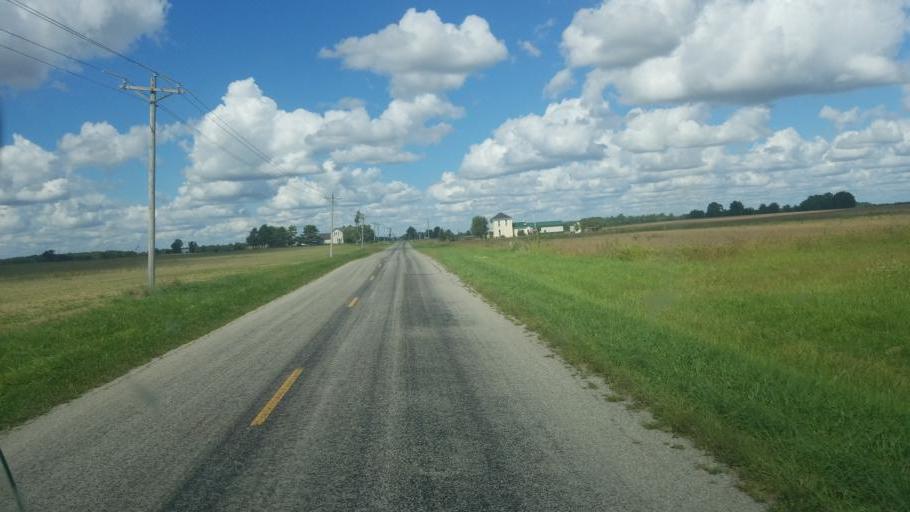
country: US
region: Ohio
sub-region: Champaign County
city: North Lewisburg
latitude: 40.3872
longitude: -83.5054
